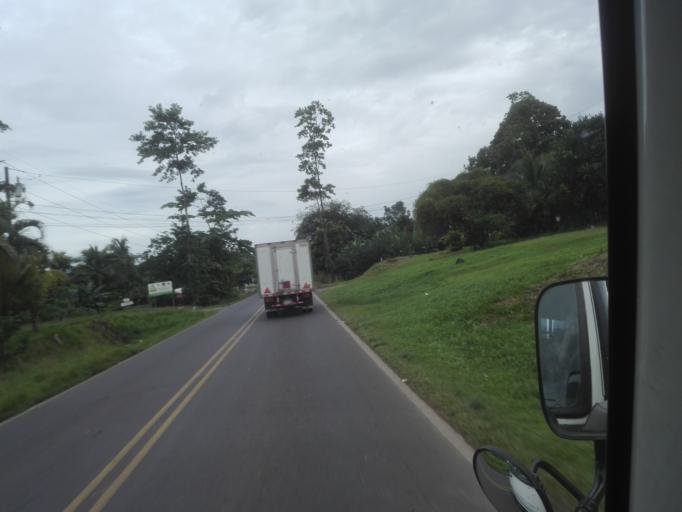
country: CR
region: San Jose
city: Dulce Nombre de Jesus
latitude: 10.3275
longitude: -83.9473
